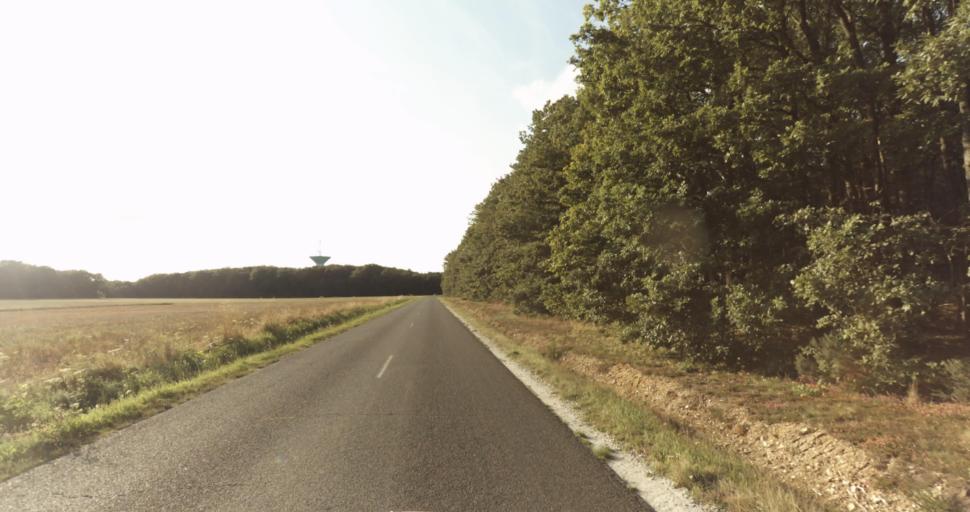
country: FR
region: Haute-Normandie
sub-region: Departement de l'Eure
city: Marcilly-sur-Eure
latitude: 48.8340
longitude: 1.3267
